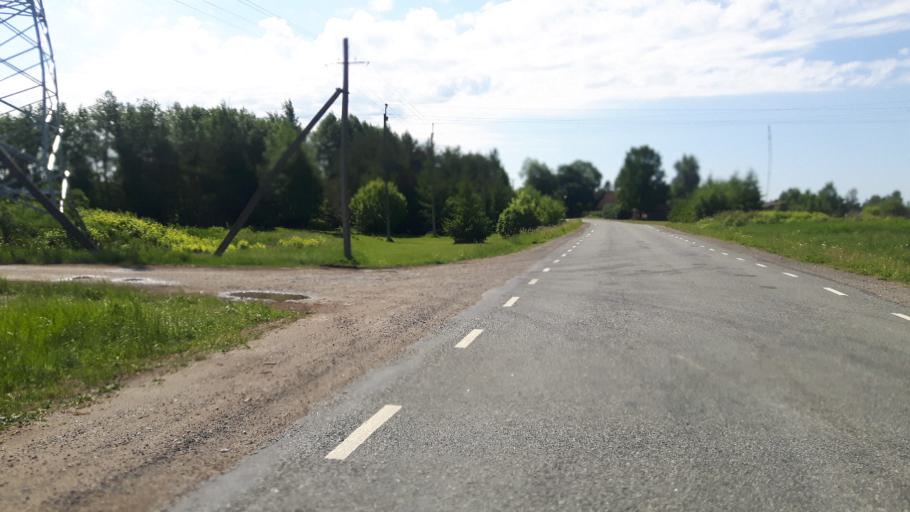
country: EE
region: Paernumaa
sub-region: Vaendra vald (alev)
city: Vandra
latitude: 58.6585
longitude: 25.0237
